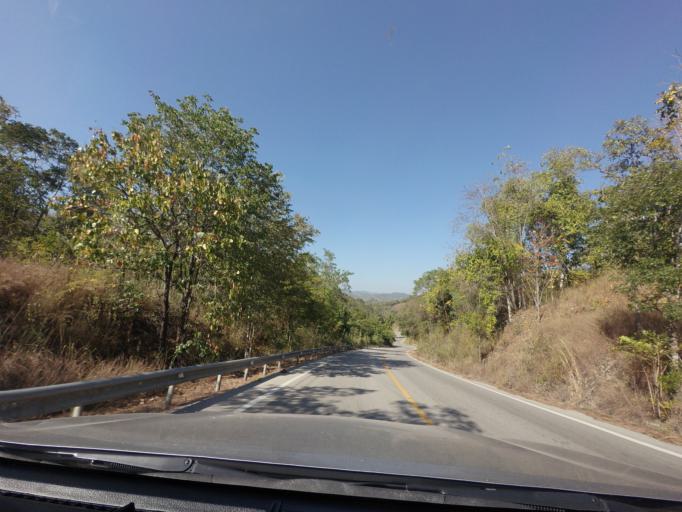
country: TH
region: Lampang
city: Chae Hom
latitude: 18.5755
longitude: 99.6269
